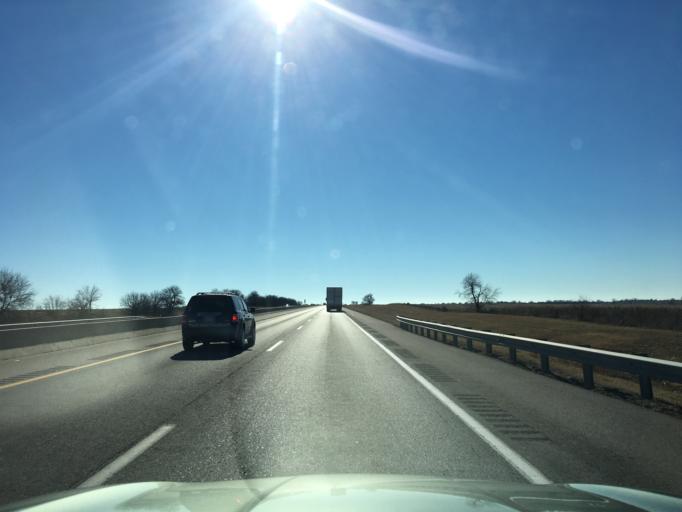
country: US
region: Kansas
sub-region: Sumner County
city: Wellington
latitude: 37.1136
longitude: -97.3388
